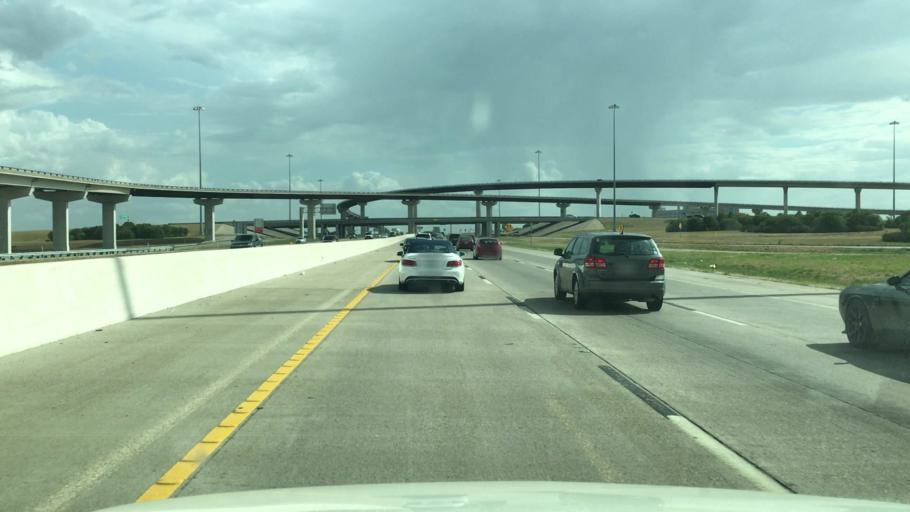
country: US
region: Texas
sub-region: McLennan County
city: Beverly Hills
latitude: 31.4967
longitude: -97.1490
